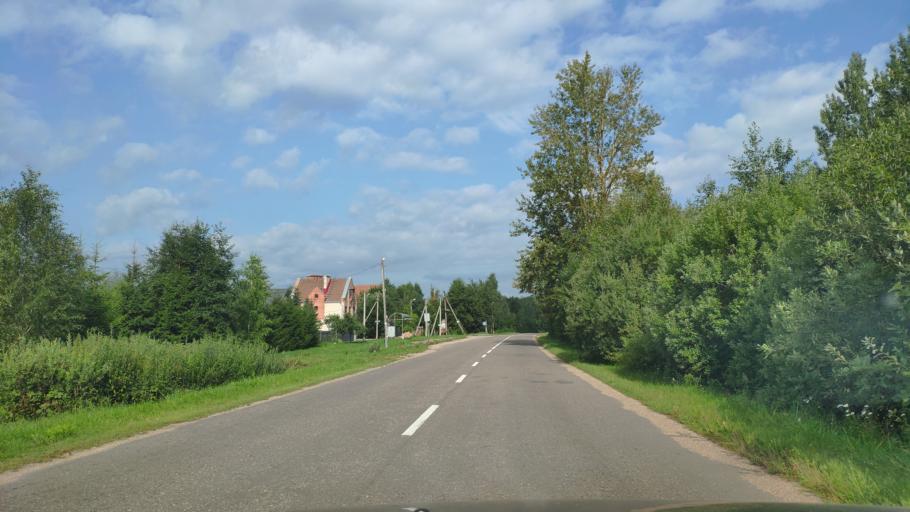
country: BY
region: Minsk
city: Khatsyezhyna
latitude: 53.8743
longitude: 27.2975
